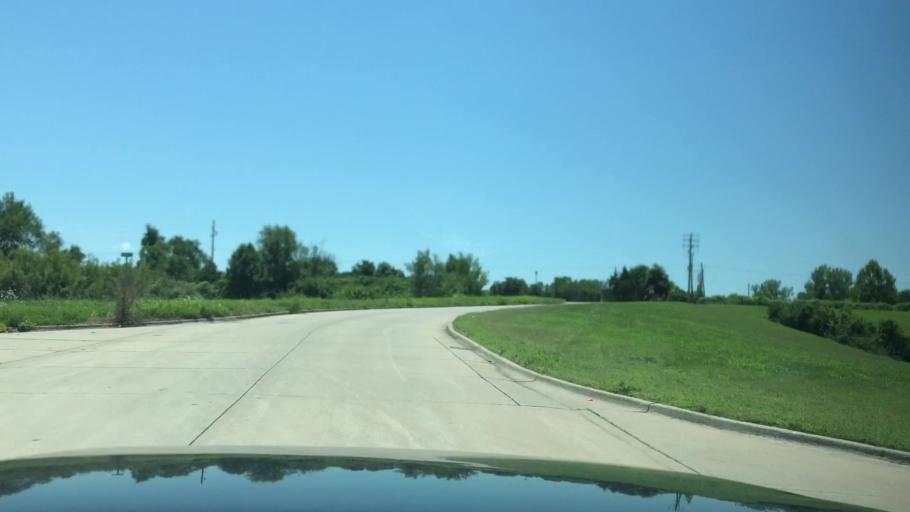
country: US
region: Illinois
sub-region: Saint Clair County
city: Alorton
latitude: 38.5545
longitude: -90.0788
